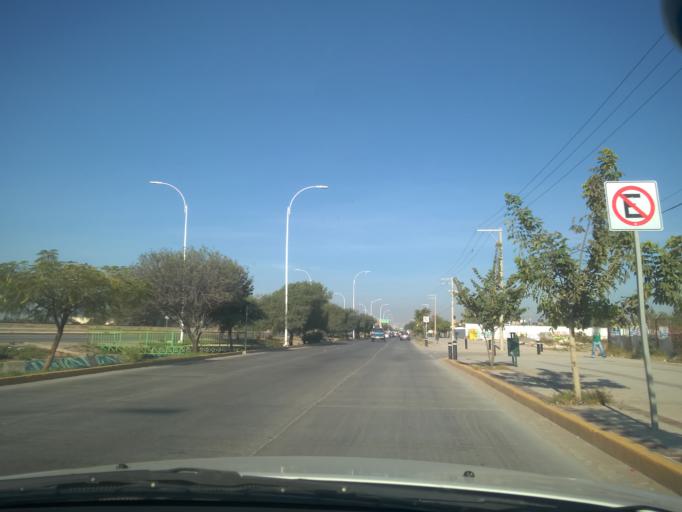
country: MX
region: Guanajuato
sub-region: Leon
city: San Jose de Duran (Los Troncoso)
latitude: 21.0718
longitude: -101.6439
